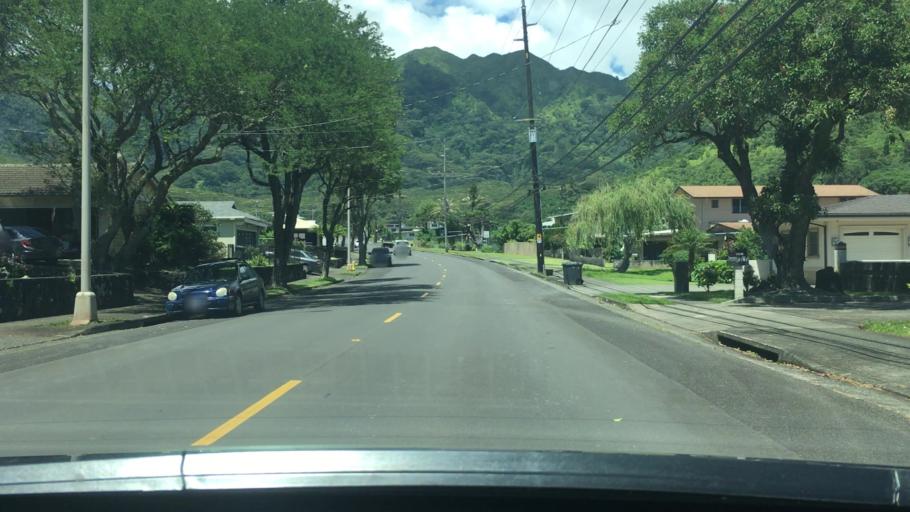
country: US
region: Hawaii
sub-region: Honolulu County
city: Honolulu
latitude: 21.3216
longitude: -157.8048
